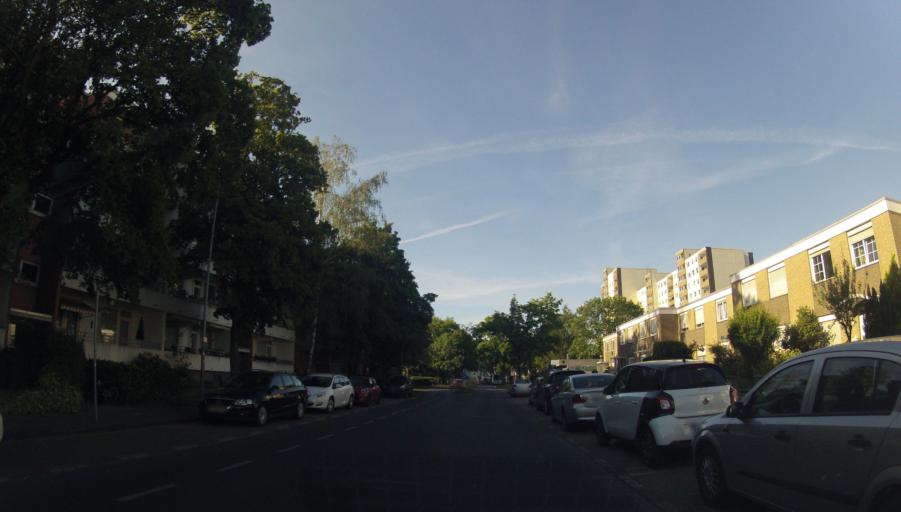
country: DE
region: North Rhine-Westphalia
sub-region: Regierungsbezirk Dusseldorf
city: Ratingen
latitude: 51.2967
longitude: 6.8178
